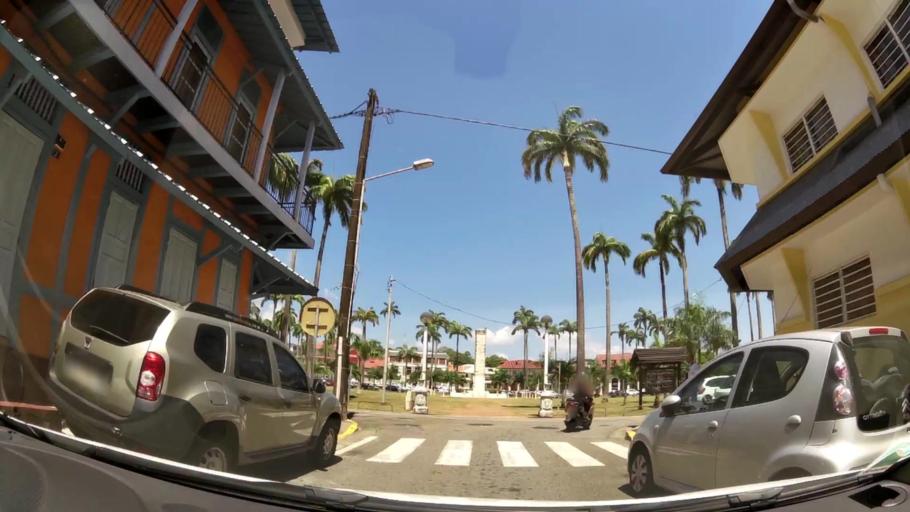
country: GF
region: Guyane
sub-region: Guyane
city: Cayenne
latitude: 4.9391
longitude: -52.3330
